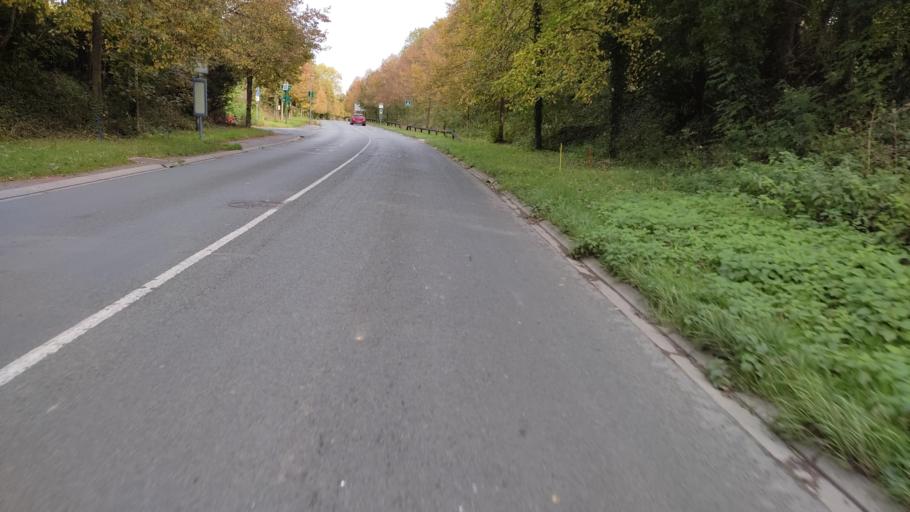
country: FR
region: Nord-Pas-de-Calais
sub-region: Departement du Pas-de-Calais
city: Saint-Laurent-Blangy
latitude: 50.2975
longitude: 2.8108
